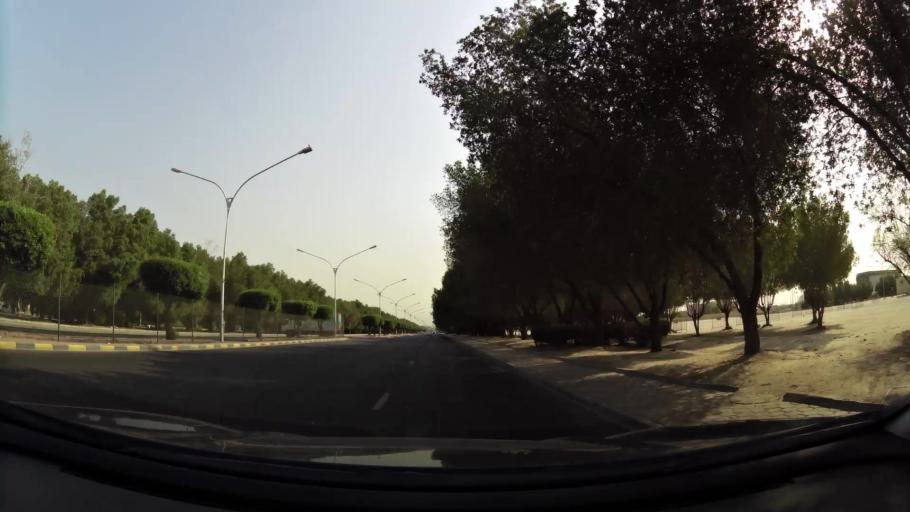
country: KW
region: Mubarak al Kabir
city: Sabah as Salim
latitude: 29.2773
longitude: 48.0632
